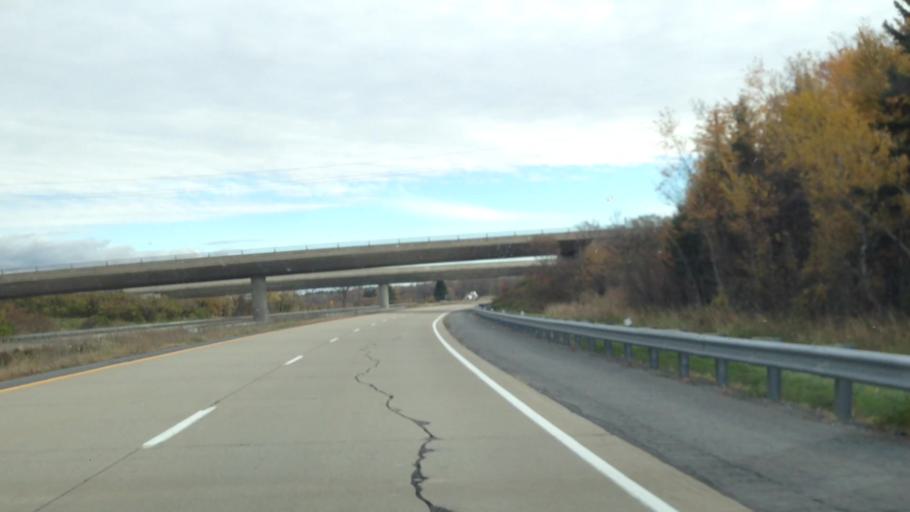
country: CA
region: Ontario
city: Hawkesbury
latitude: 45.5643
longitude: -74.5068
